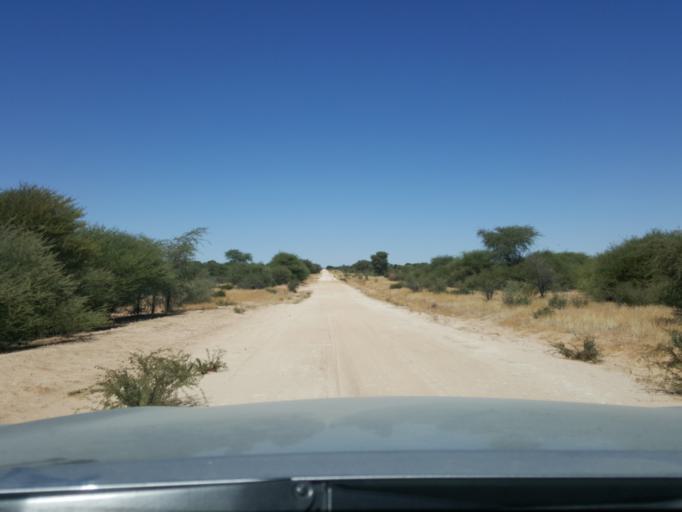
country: BW
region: Kgalagadi
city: Hukuntsi
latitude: -23.9926
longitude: 21.2106
